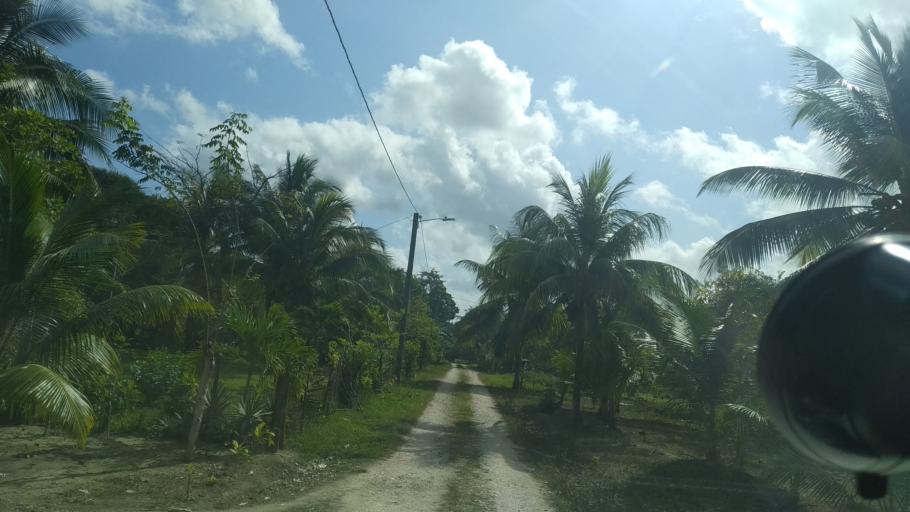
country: BZ
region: Stann Creek
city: Placencia
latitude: 16.4720
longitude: -88.6239
